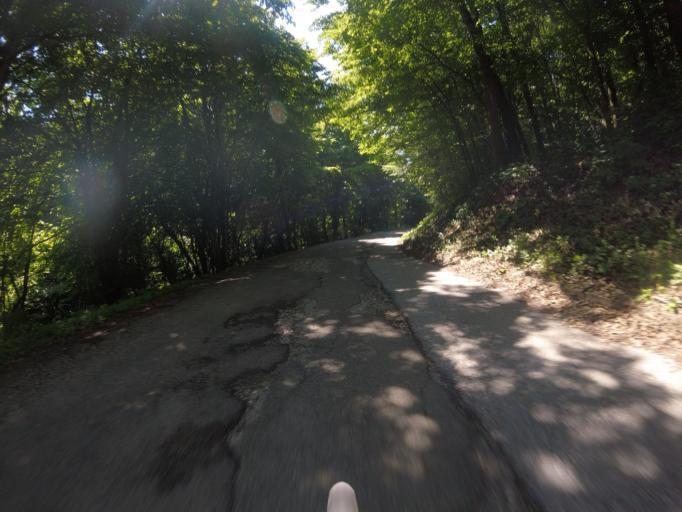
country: SI
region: Kostanjevica na Krki
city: Kostanjevica na Krki
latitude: 45.7937
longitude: 15.4935
